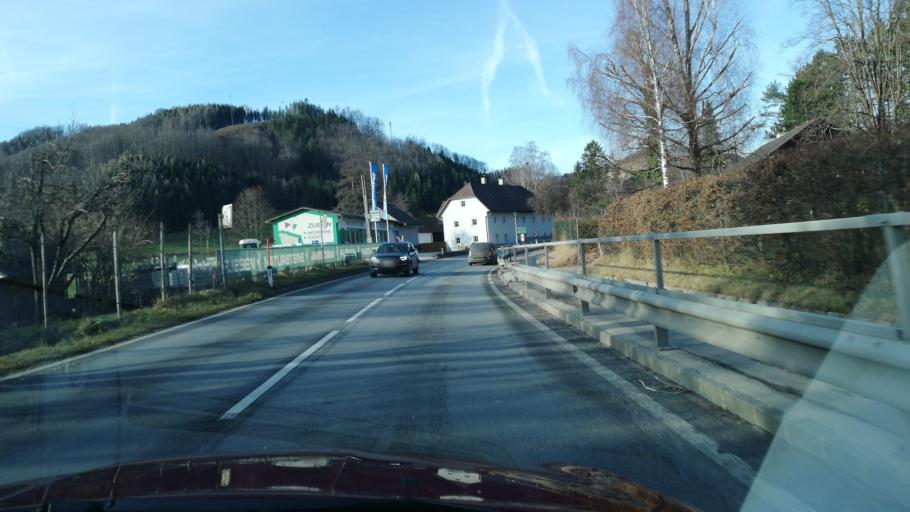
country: AT
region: Upper Austria
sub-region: Politischer Bezirk Kirchdorf an der Krems
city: Micheldorf in Oberoesterreich
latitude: 47.8521
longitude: 14.1526
